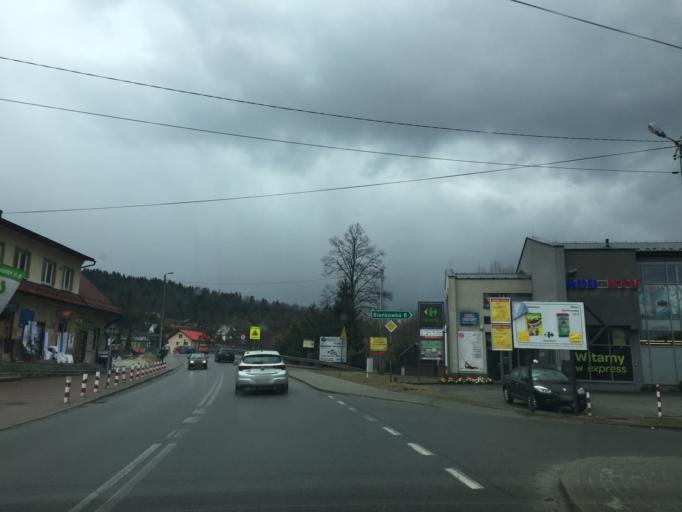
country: PL
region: Lesser Poland Voivodeship
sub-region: Powiat suski
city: Budzow
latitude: 49.7756
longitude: 19.6721
